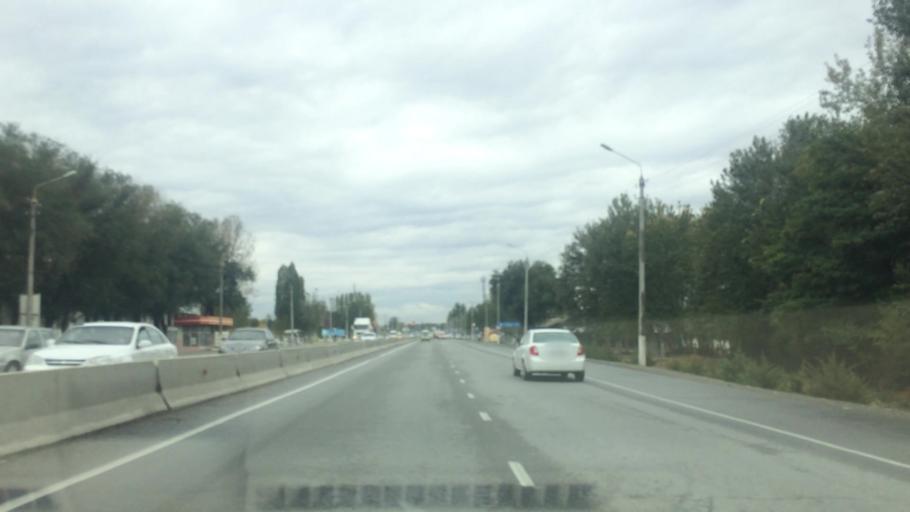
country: UZ
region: Jizzax
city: Jizzax
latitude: 39.9847
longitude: 67.5746
